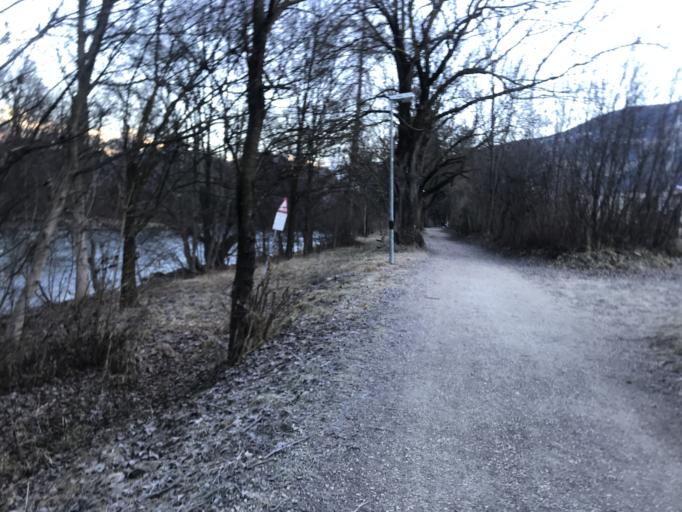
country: IT
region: Trentino-Alto Adige
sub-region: Bolzano
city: Bressanone
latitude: 46.7037
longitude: 11.6535
